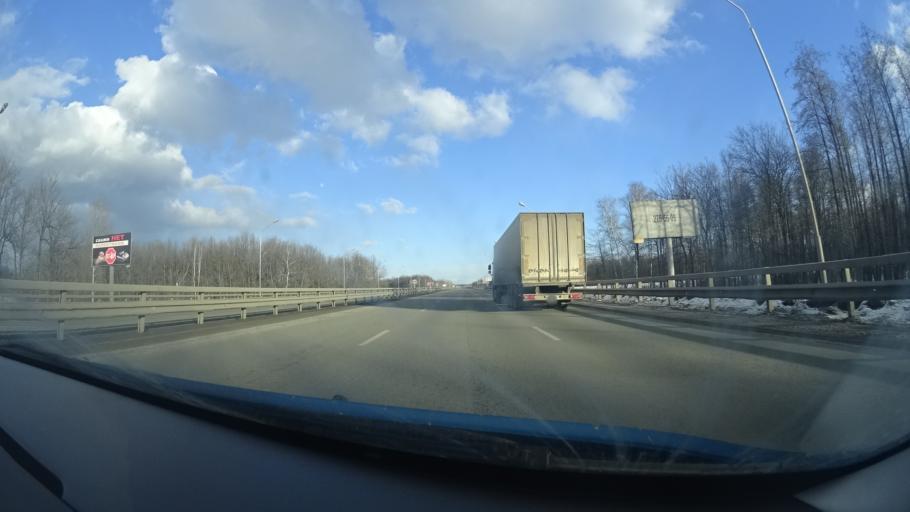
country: RU
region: Bashkortostan
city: Avdon
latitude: 54.6685
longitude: 55.8456
